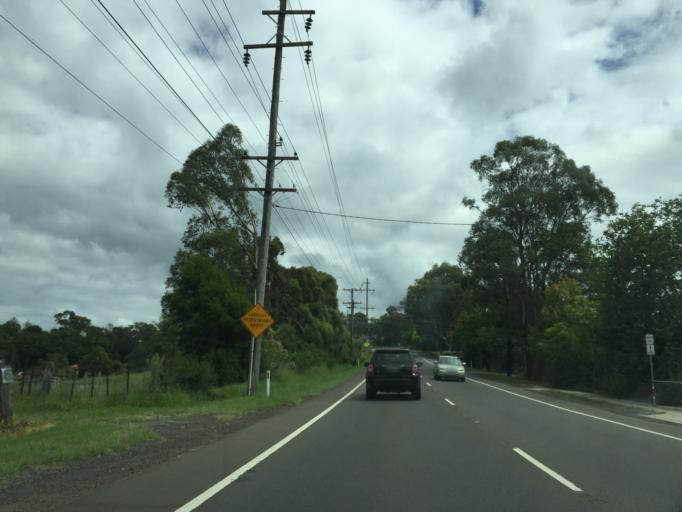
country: AU
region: New South Wales
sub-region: Hawkesbury
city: Richmond
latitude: -33.5532
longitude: 150.6953
